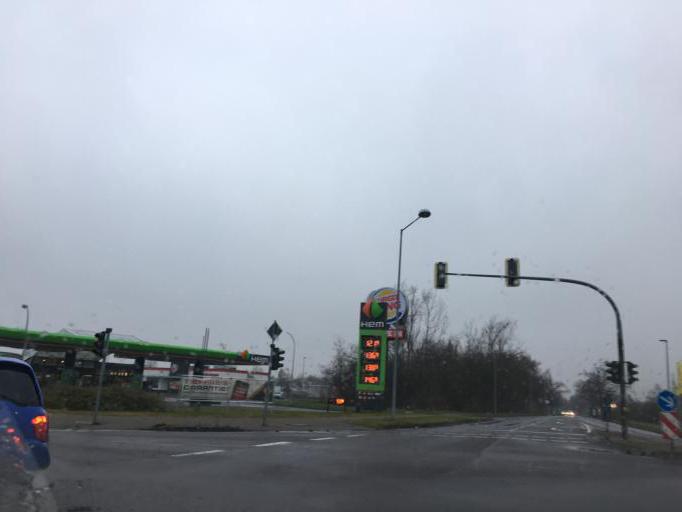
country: DE
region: Saxony-Anhalt
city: Haldensleben I
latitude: 52.2818
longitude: 11.4335
